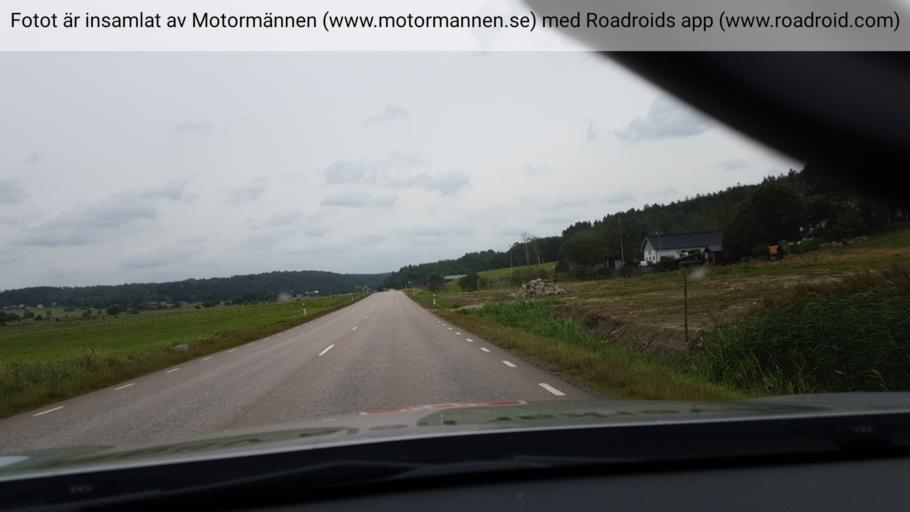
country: SE
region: Vaestra Goetaland
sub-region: Molndal
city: Lindome
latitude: 57.5920
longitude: 12.1371
